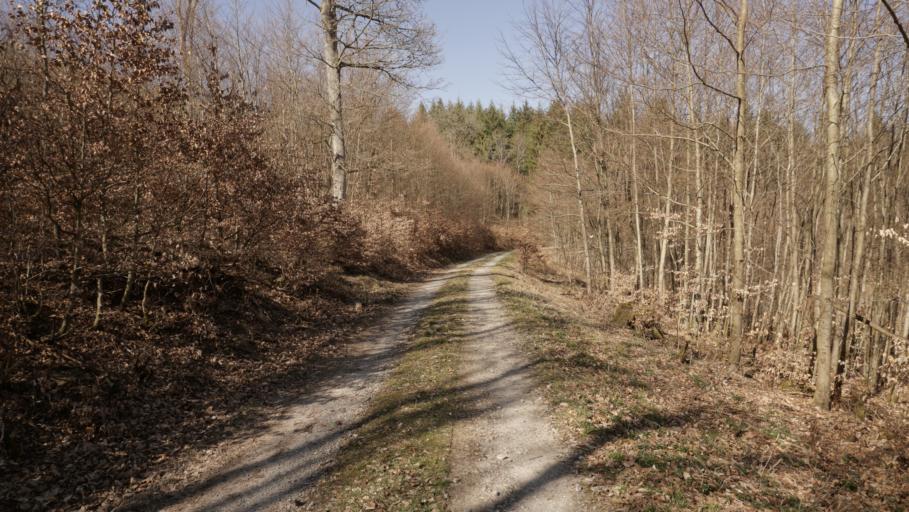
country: DE
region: Baden-Wuerttemberg
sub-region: Karlsruhe Region
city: Fahrenbach
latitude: 49.4387
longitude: 9.1253
